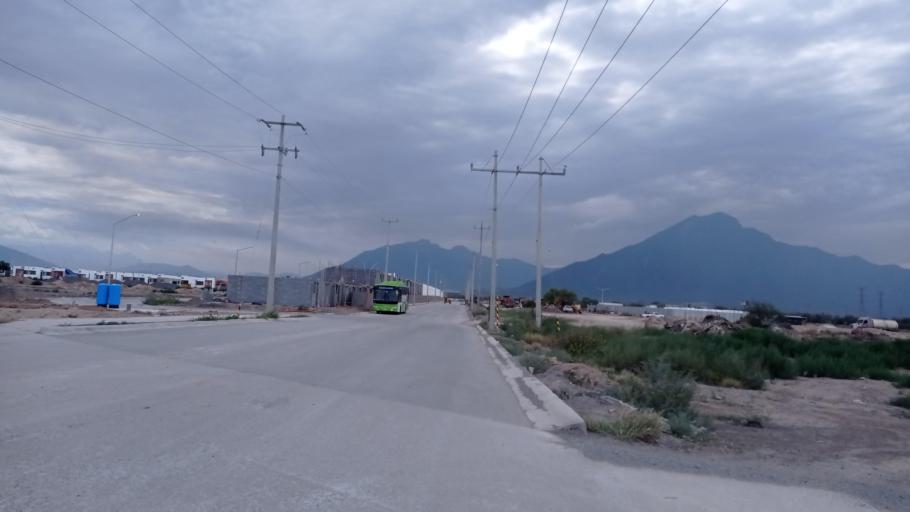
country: MX
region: Nuevo Leon
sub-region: Salinas Victoria
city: Simeprodeso (Colectivo Nuevo)
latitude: 25.8766
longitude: -100.3203
